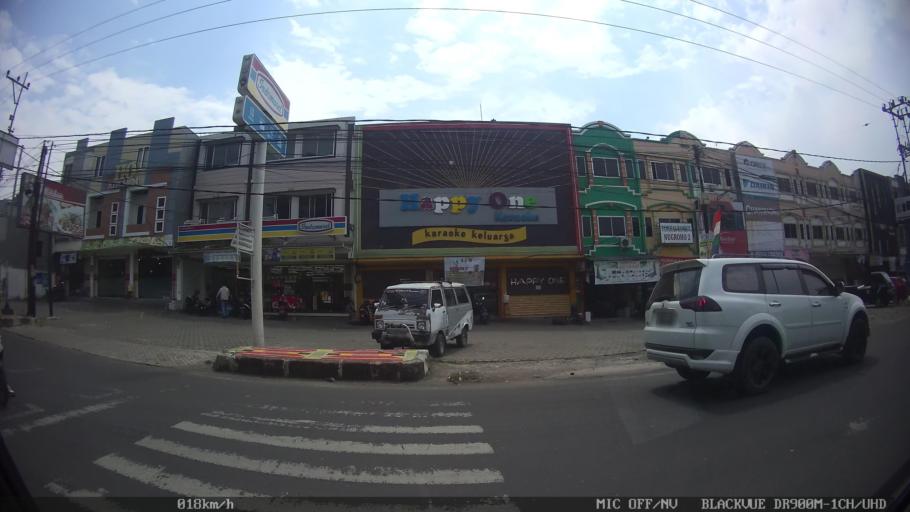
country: ID
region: Lampung
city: Bandarlampung
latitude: -5.4337
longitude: 105.2626
